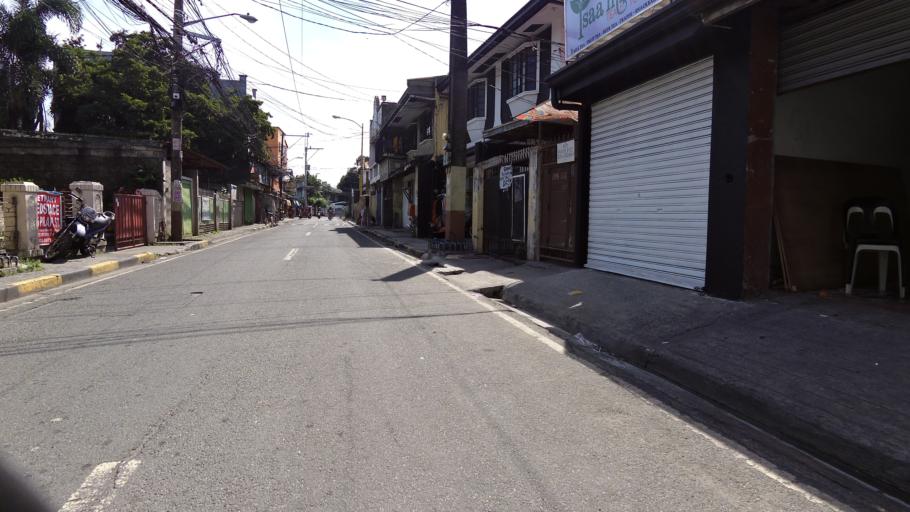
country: PH
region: Calabarzon
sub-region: Province of Rizal
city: Pateros
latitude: 14.5668
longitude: 121.0832
